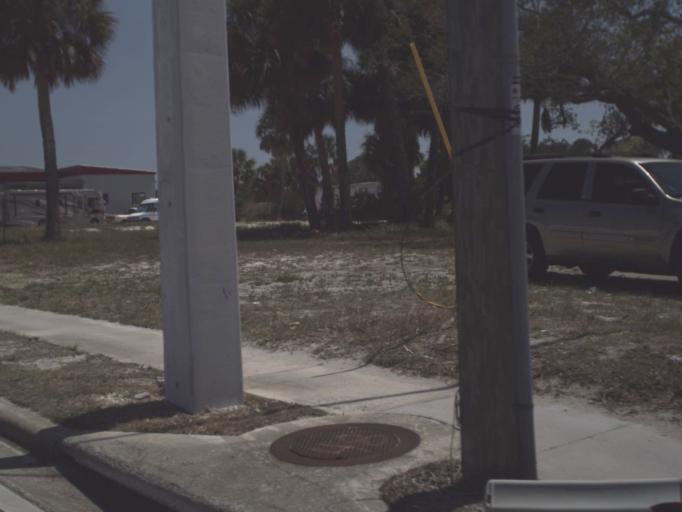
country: US
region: Florida
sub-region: Brevard County
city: Melbourne
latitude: 28.0683
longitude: -80.6000
